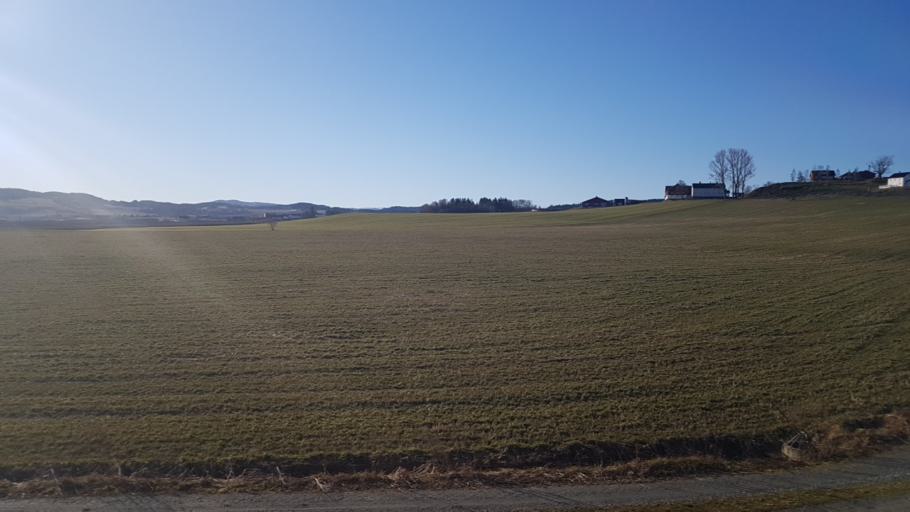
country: NO
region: Nord-Trondelag
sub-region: Levanger
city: Skogn
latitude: 63.6943
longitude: 11.1794
